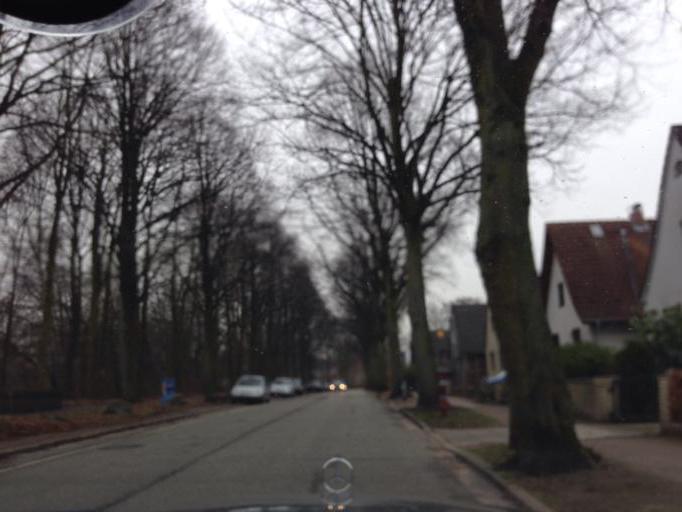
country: DE
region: Hamburg
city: Farmsen-Berne
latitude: 53.5973
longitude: 10.1071
